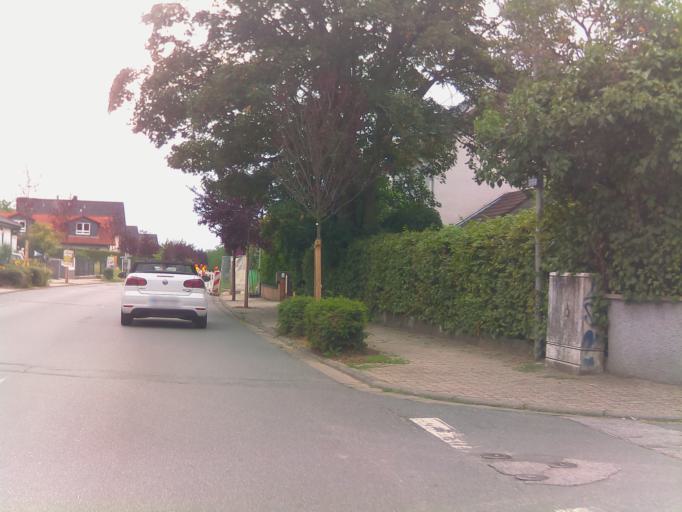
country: DE
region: Hesse
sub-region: Regierungsbezirk Darmstadt
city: Bickenbach
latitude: 49.7516
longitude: 8.6311
